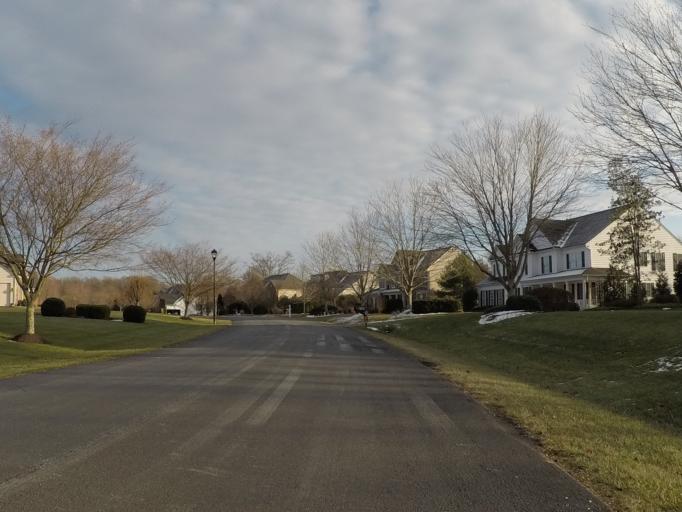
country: US
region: Maryland
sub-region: Howard County
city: Columbia
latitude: 39.2826
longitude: -76.9031
